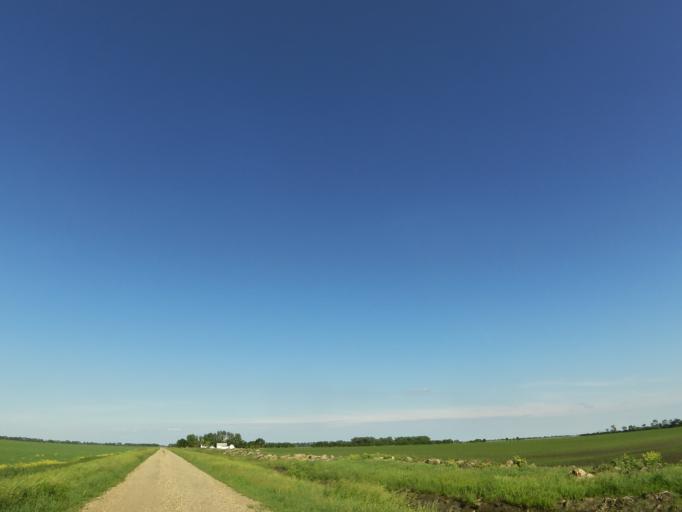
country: US
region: North Dakota
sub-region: Walsh County
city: Grafton
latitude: 48.3975
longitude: -97.2555
